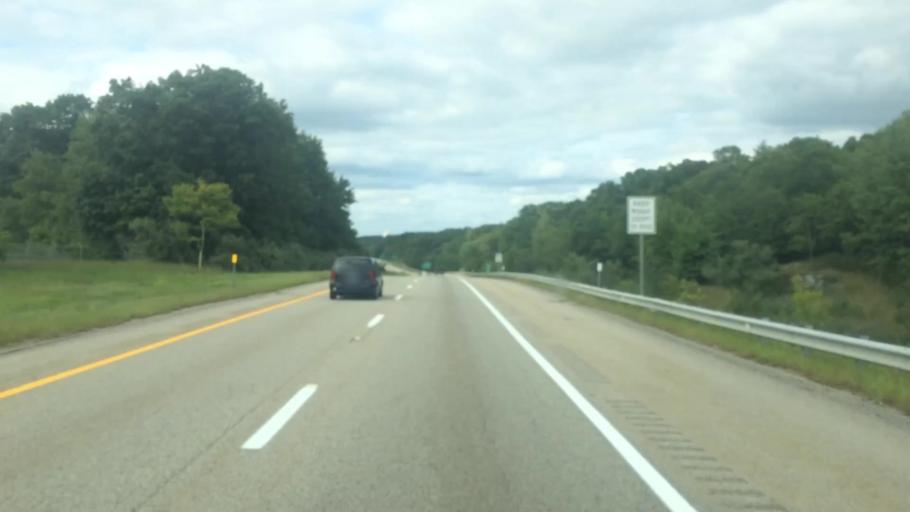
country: US
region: Rhode Island
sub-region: Providence County
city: Cumberland Hill
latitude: 41.9491
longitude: -71.4818
